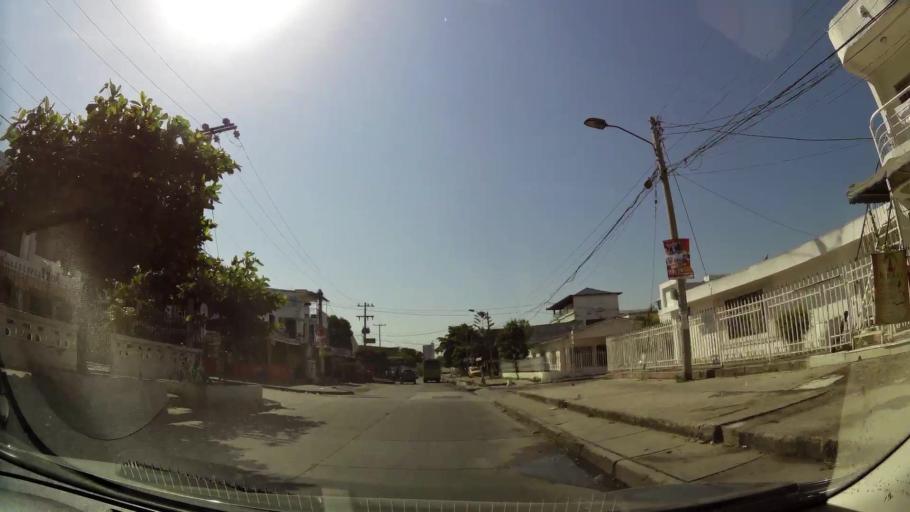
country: CO
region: Bolivar
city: Cartagena
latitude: 10.3906
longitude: -75.5036
